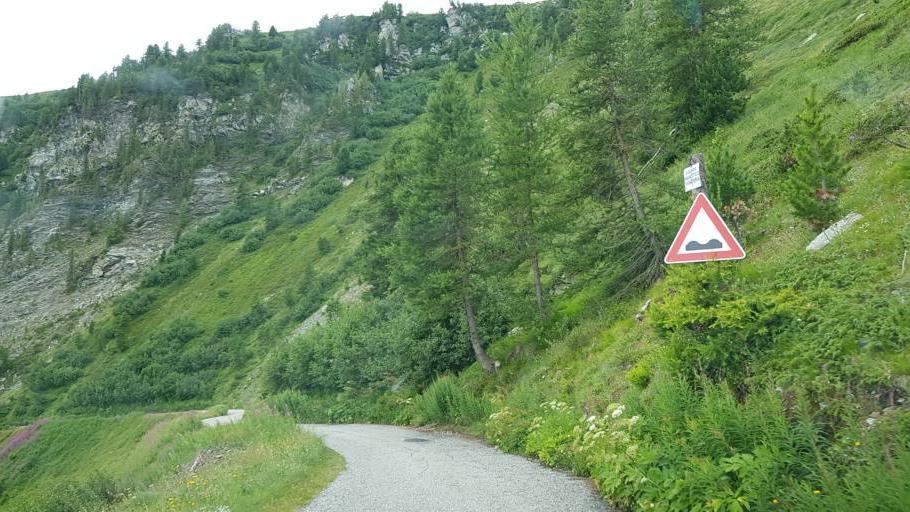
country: IT
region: Piedmont
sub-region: Provincia di Cuneo
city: Serre
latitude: 44.5502
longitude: 7.1268
